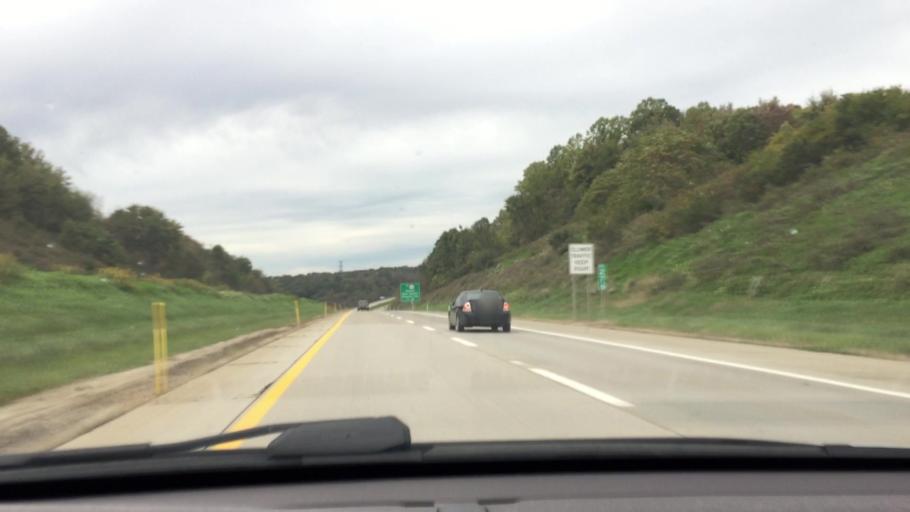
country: US
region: Pennsylvania
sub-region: Beaver County
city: Big Beaver
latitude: 40.8110
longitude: -80.3663
